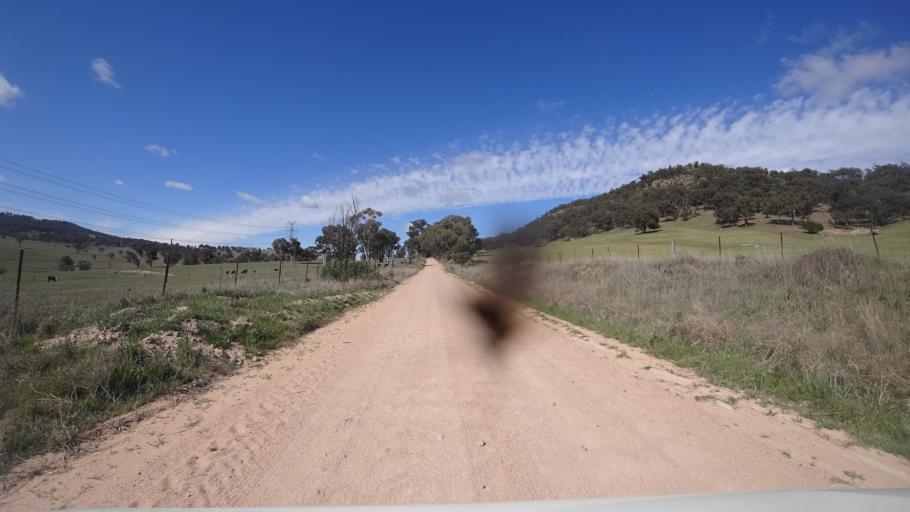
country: AU
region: New South Wales
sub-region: Lithgow
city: Portland
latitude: -33.5272
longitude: 149.9350
